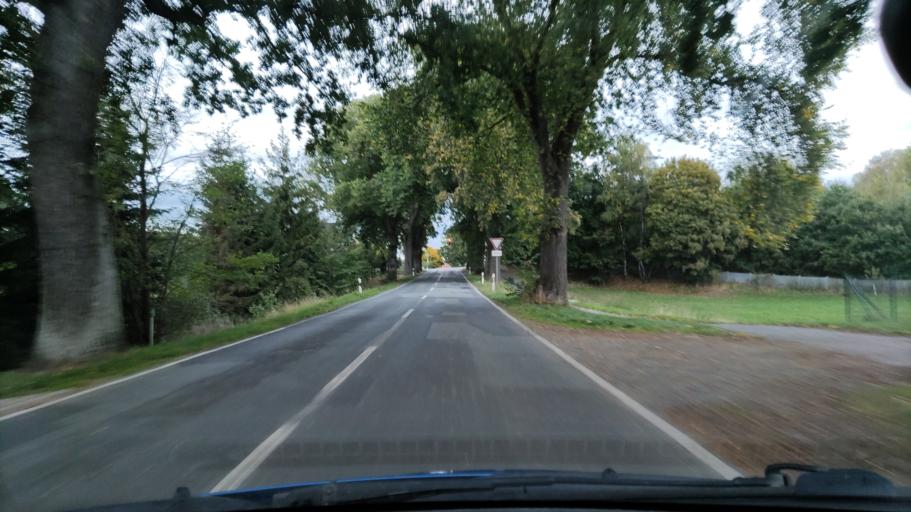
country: DE
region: Mecklenburg-Vorpommern
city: Lubtheen
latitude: 53.3925
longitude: 10.9653
